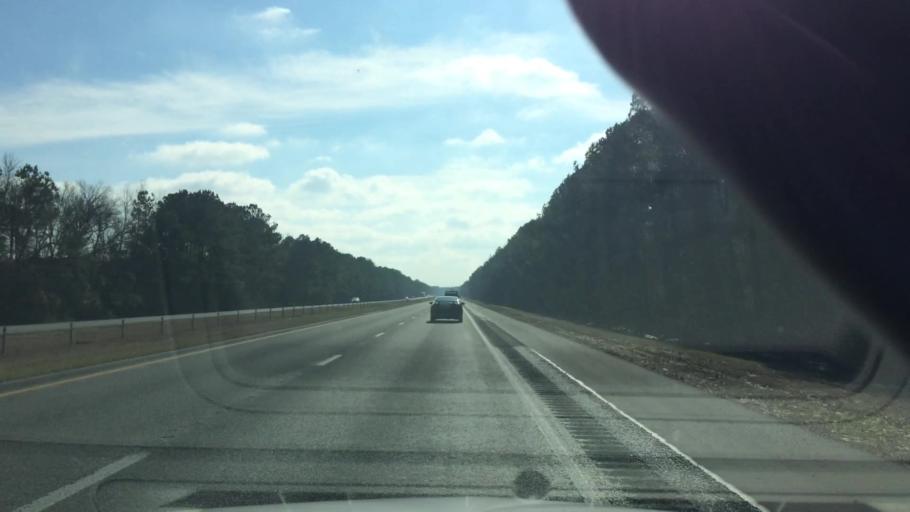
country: US
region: North Carolina
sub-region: Duplin County
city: Wallace
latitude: 34.7299
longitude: -77.9450
